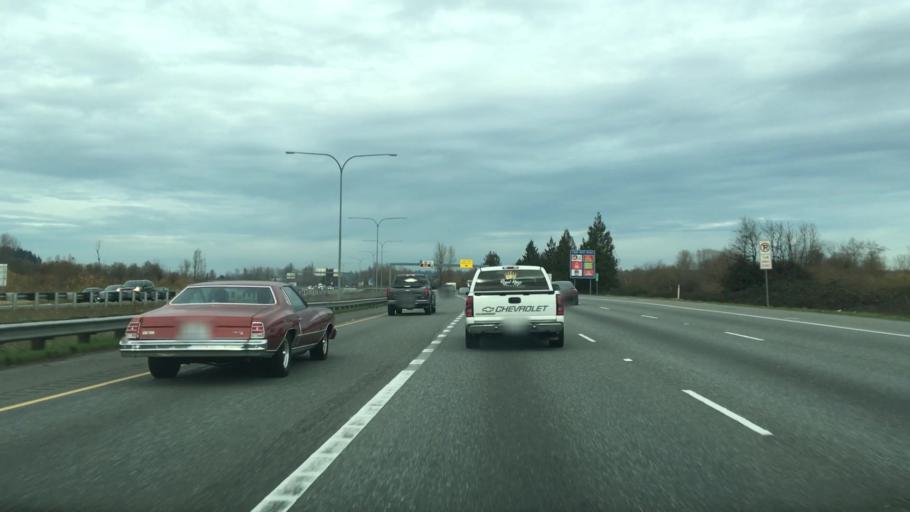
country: US
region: Washington
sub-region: King County
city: Auburn
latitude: 47.3104
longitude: -122.2464
